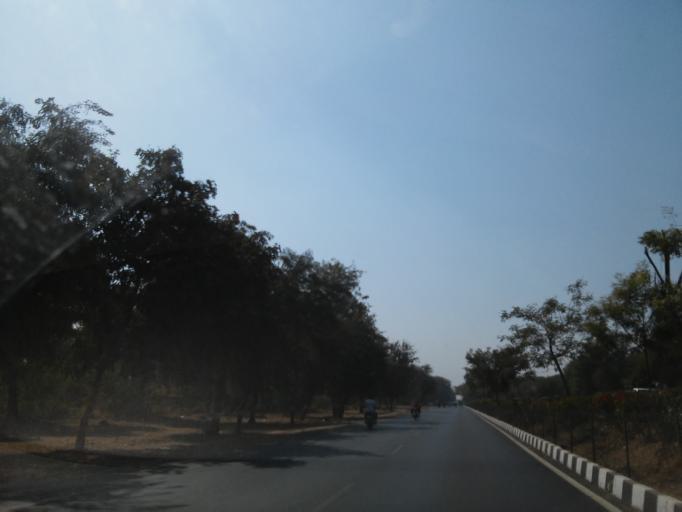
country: IN
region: Gujarat
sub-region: Gandhinagar
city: Adalaj
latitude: 23.1822
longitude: 72.5958
